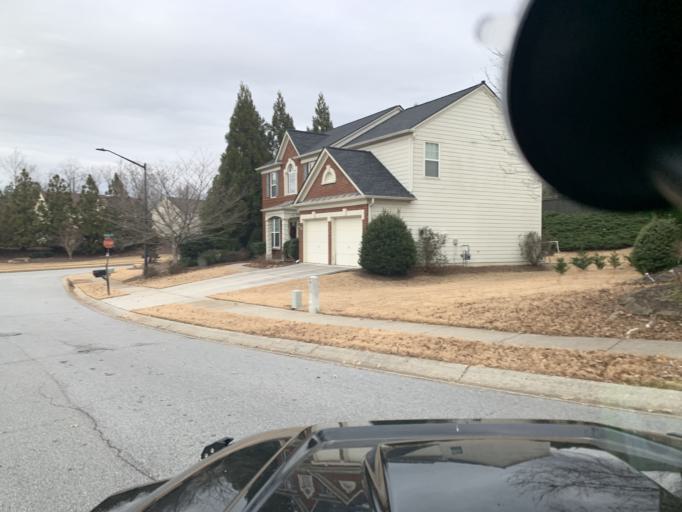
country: US
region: Georgia
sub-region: Cherokee County
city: Woodstock
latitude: 34.0978
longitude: -84.4594
